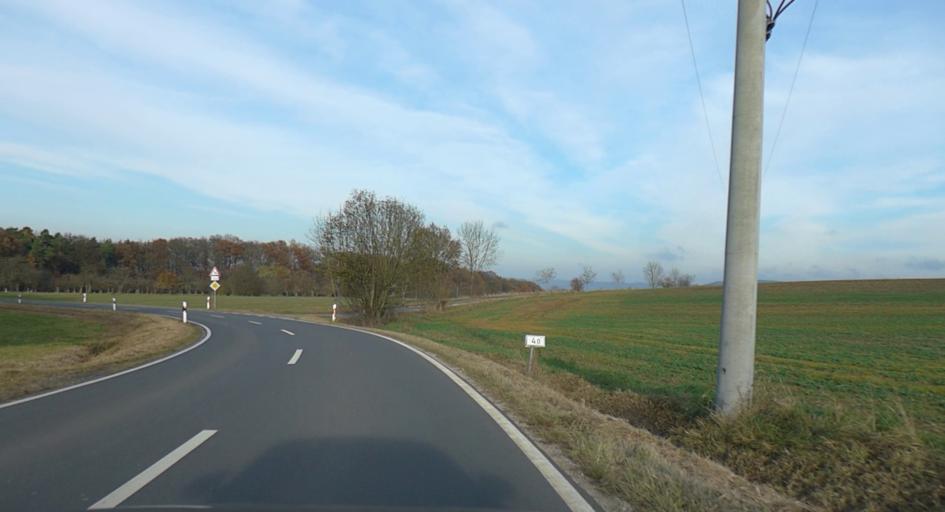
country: DE
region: Bavaria
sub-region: Regierungsbezirk Mittelfranken
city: Bubenreuth
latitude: 49.6191
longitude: 11.0309
